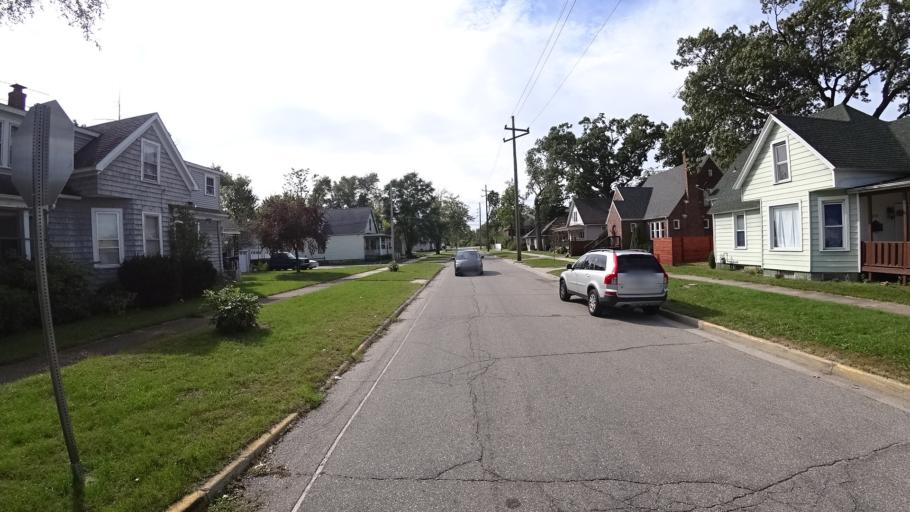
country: US
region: Indiana
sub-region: LaPorte County
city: Michigan City
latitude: 41.7149
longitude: -86.8857
